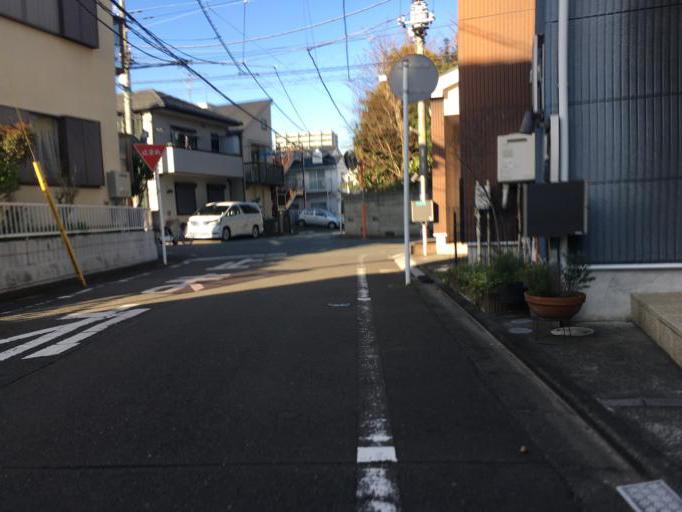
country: JP
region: Tokyo
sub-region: Machida-shi
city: Machida
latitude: 35.5697
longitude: 139.3861
